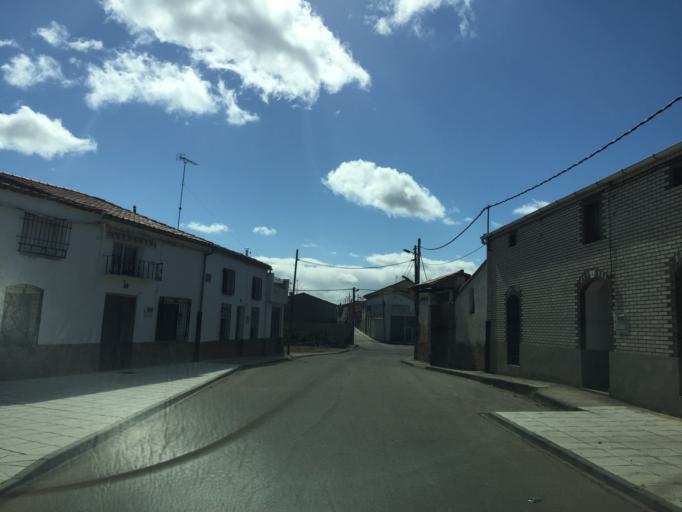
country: ES
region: Castille and Leon
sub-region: Provincia de Zamora
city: Montamarta
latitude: 41.6494
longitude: -5.8060
